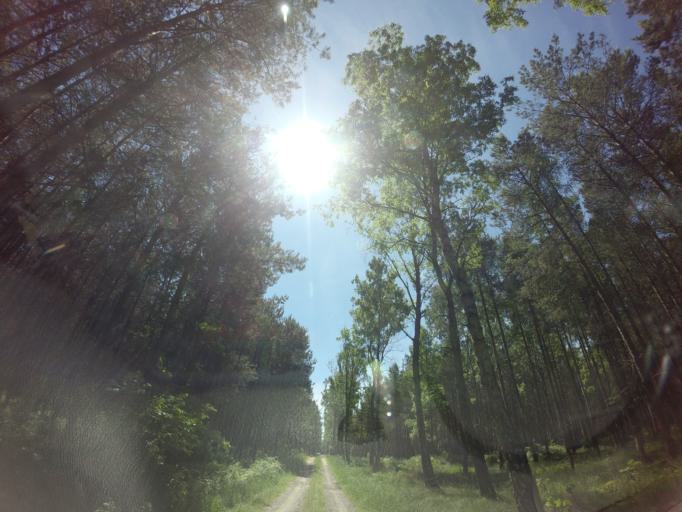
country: PL
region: West Pomeranian Voivodeship
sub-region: Powiat choszczenski
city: Drawno
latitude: 53.2619
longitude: 15.7458
